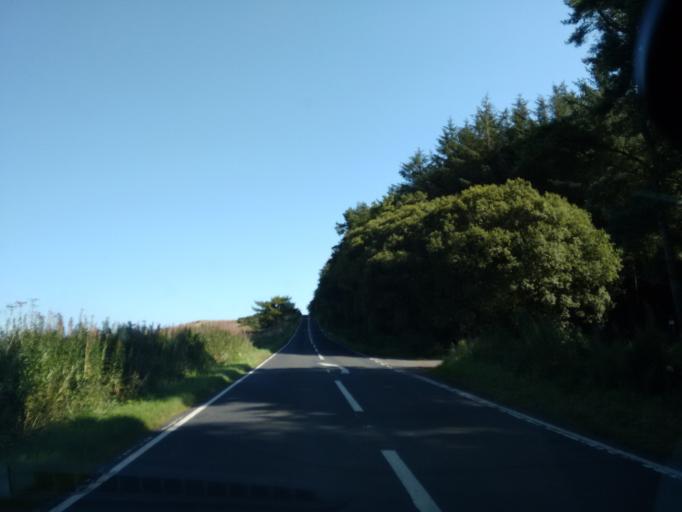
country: GB
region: England
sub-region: Northumberland
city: Corbridge
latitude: 55.0166
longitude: -2.0525
